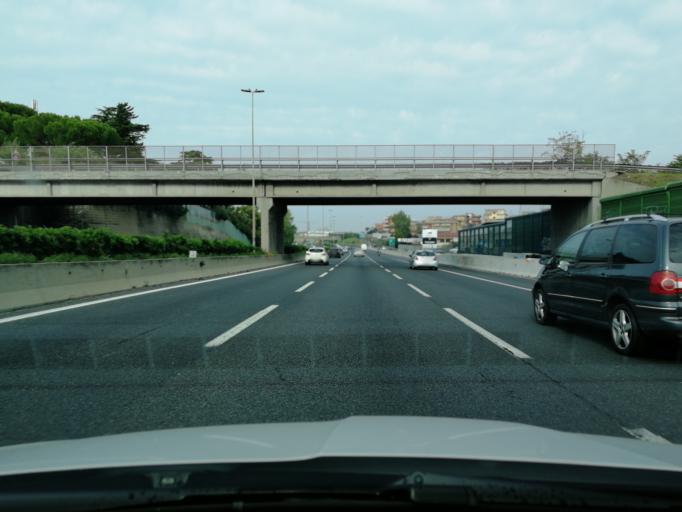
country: IT
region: Latium
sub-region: Citta metropolitana di Roma Capitale
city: Setteville
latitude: 41.8855
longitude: 12.6129
